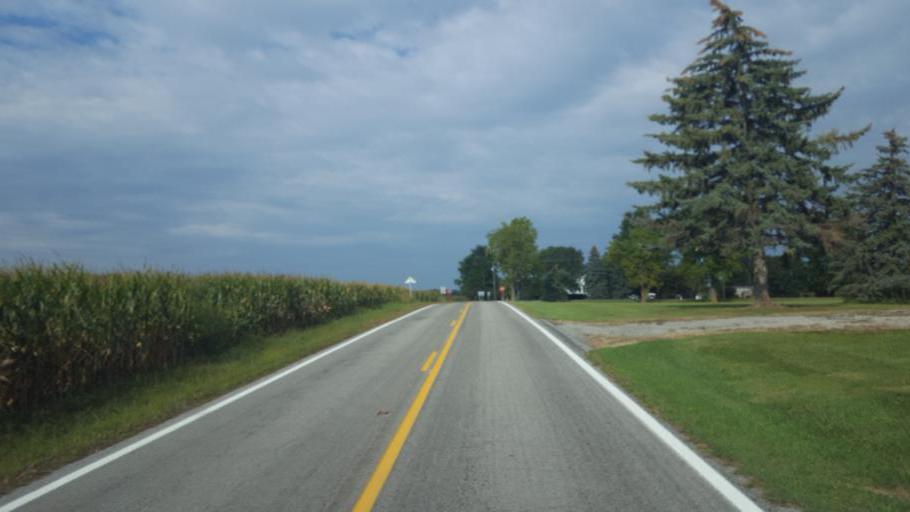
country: US
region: Ohio
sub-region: Marion County
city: Marion
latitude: 40.7174
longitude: -83.1240
